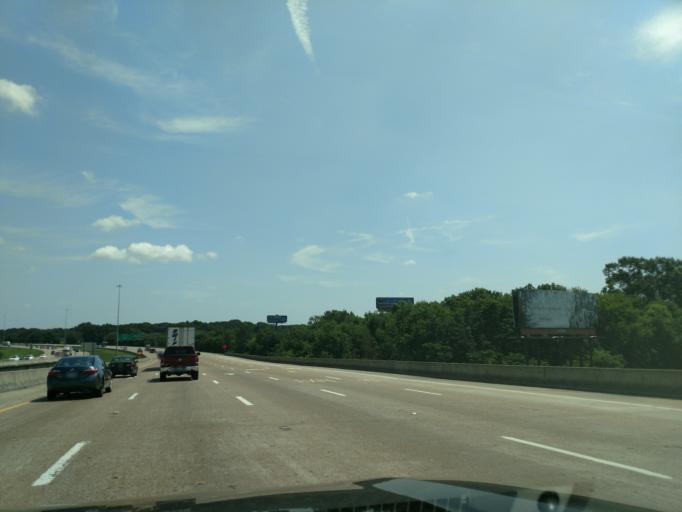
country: US
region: Mississippi
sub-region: Hinds County
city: Jackson
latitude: 32.2840
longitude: -90.1702
